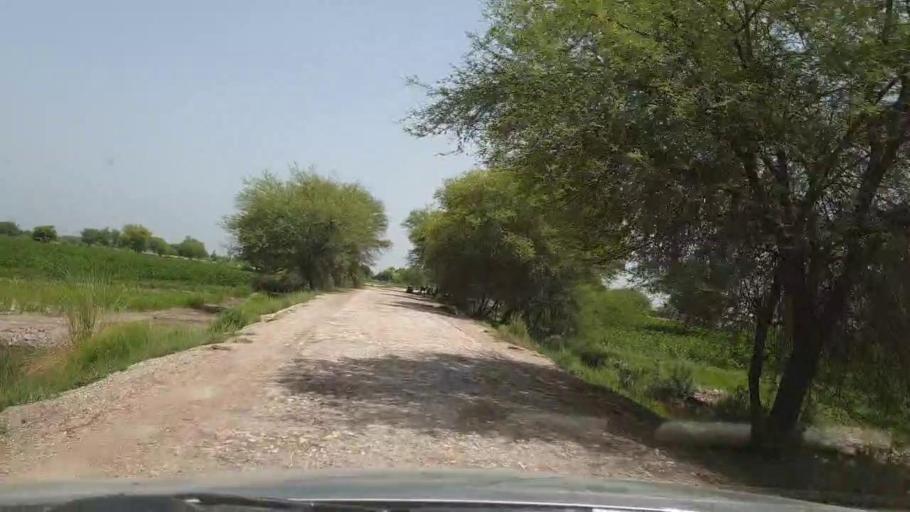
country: PK
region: Sindh
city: Pano Aqil
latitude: 27.8237
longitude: 69.2180
